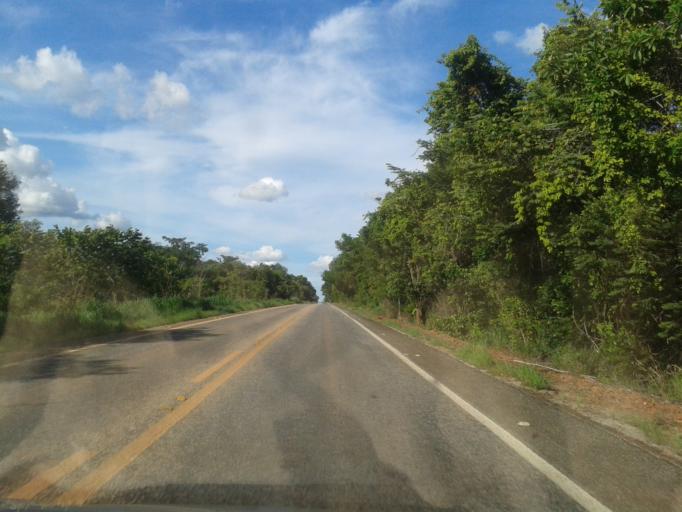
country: BR
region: Goias
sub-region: Mozarlandia
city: Mozarlandia
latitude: -14.4482
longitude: -50.4614
